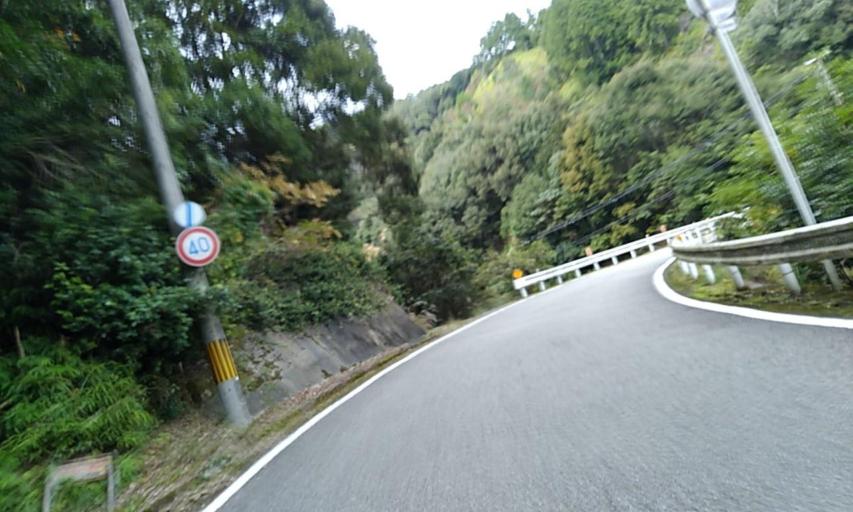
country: JP
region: Wakayama
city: Shingu
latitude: 33.5418
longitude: 135.8298
